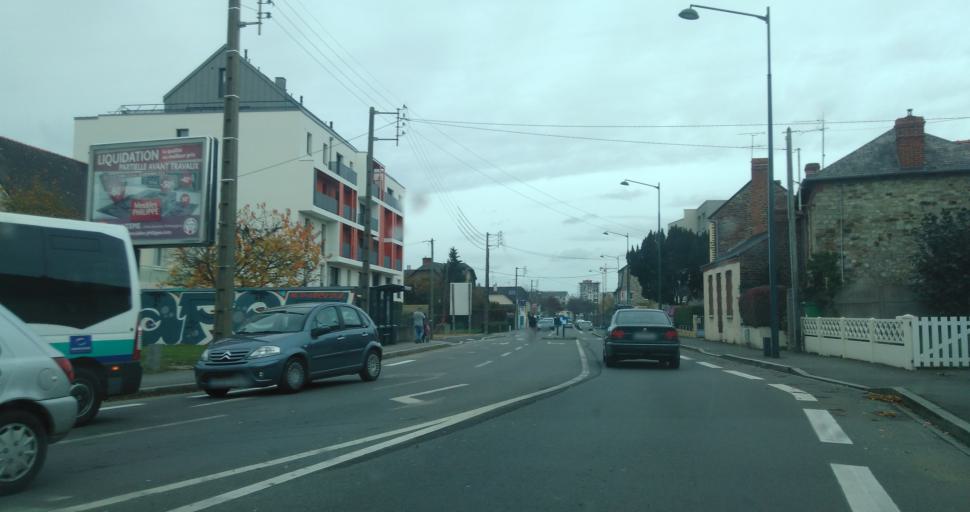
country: FR
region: Brittany
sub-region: Departement d'Ille-et-Vilaine
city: Rennes
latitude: 48.1005
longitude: -1.6498
